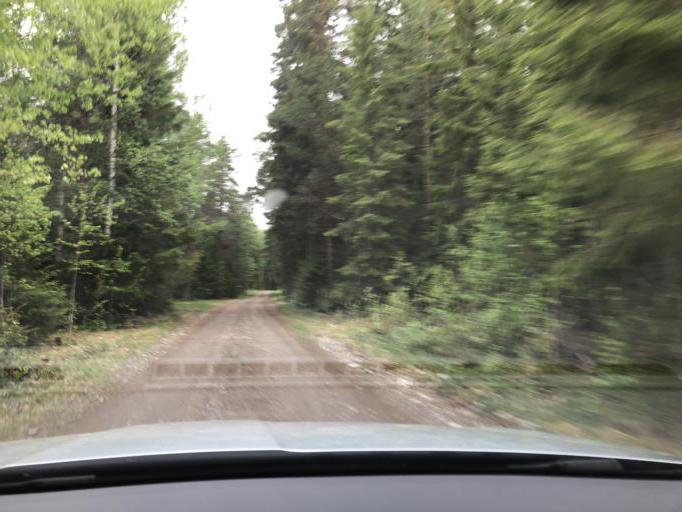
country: SE
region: Norrbotten
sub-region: Pitea Kommun
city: Roknas
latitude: 65.3937
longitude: 21.2681
